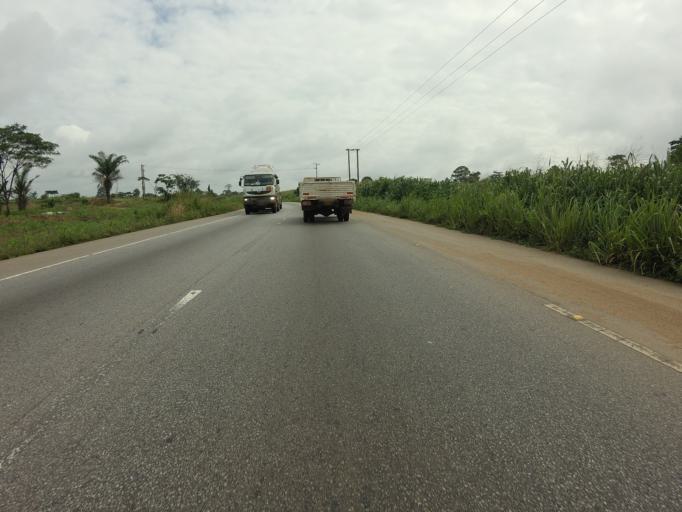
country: GH
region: Ashanti
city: Tafo
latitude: 6.9843
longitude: -1.6882
